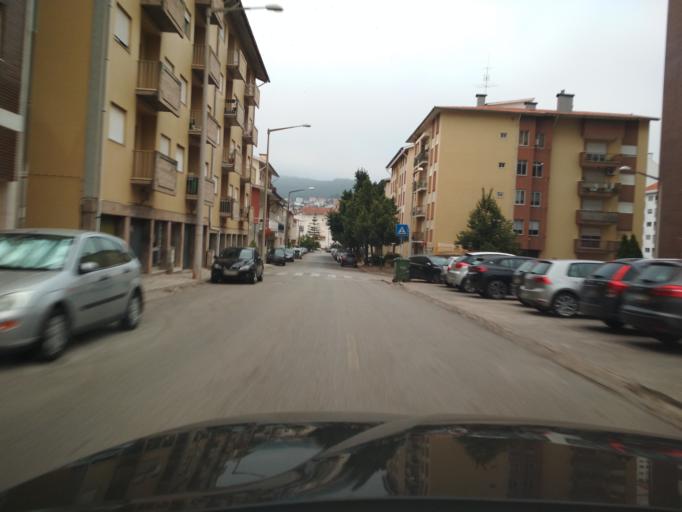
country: PT
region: Coimbra
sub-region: Coimbra
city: Coimbra
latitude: 40.1971
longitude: -8.4060
